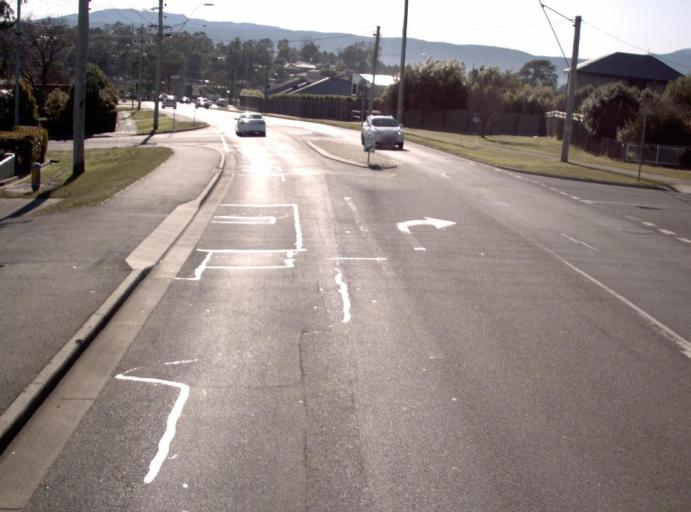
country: AU
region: Tasmania
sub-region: Launceston
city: Summerhill
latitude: -41.4726
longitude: 147.1307
